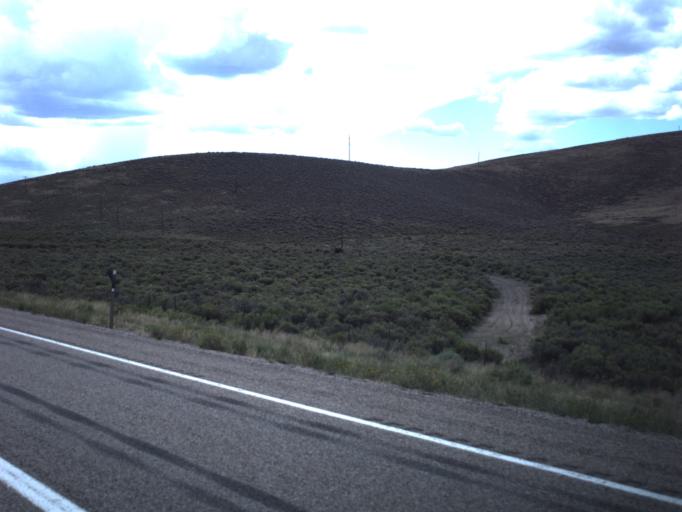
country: US
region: Utah
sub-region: Piute County
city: Junction
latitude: 38.2108
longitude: -112.2244
